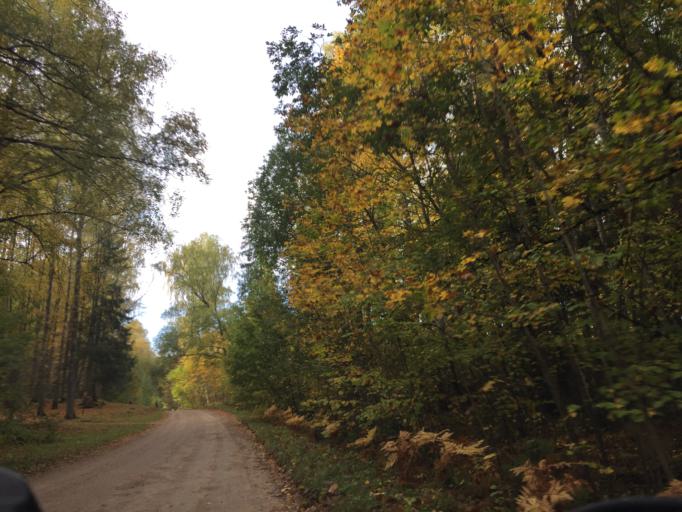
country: LV
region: Jaunpils
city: Jaunpils
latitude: 56.6157
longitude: 23.0283
